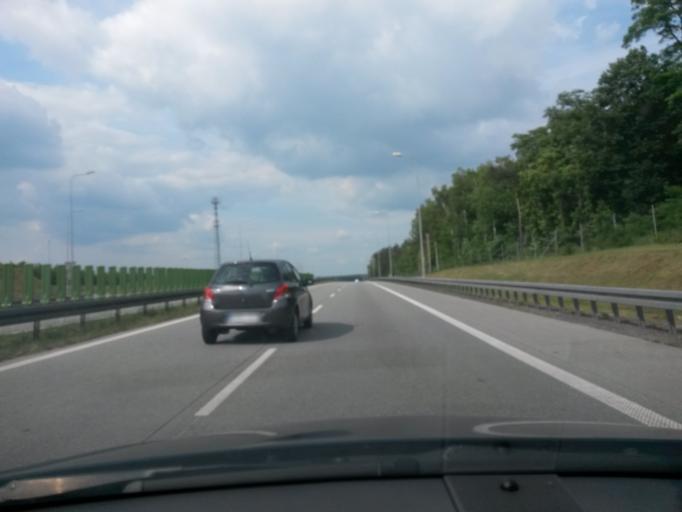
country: PL
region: Lodz Voivodeship
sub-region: Powiat rawski
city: Rawa Mazowiecka
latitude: 51.8185
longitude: 20.3166
